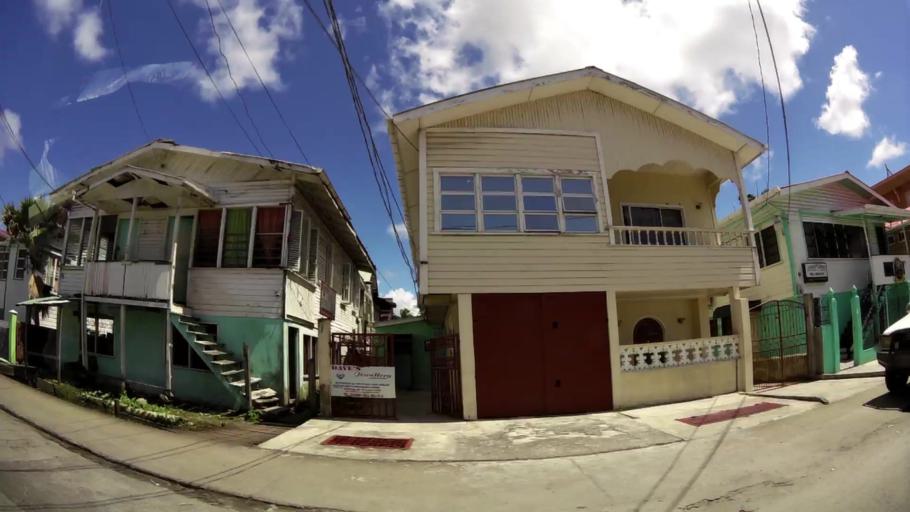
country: GY
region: Demerara-Mahaica
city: Georgetown
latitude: 6.8031
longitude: -58.1534
